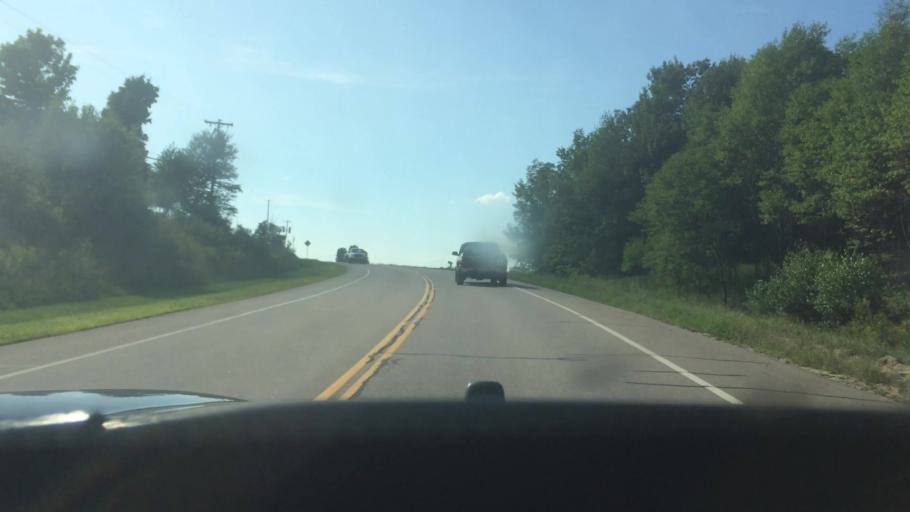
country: US
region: New York
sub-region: Franklin County
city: Malone
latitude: 44.8503
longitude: -74.2014
